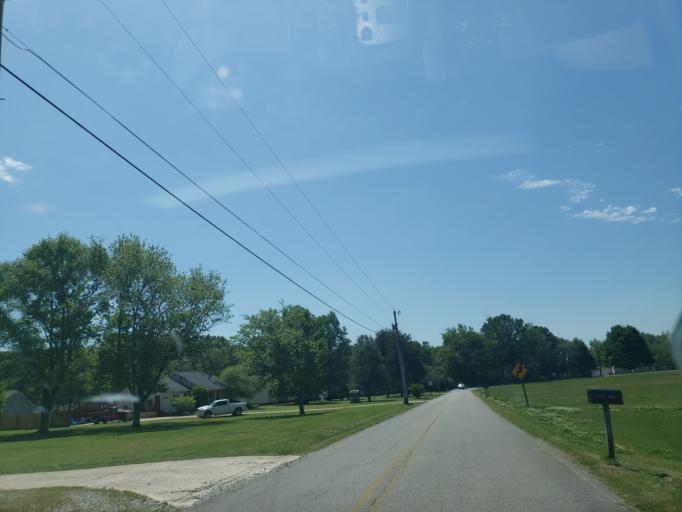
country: US
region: Alabama
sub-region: Madison County
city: Hazel Green
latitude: 34.9520
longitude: -86.5342
